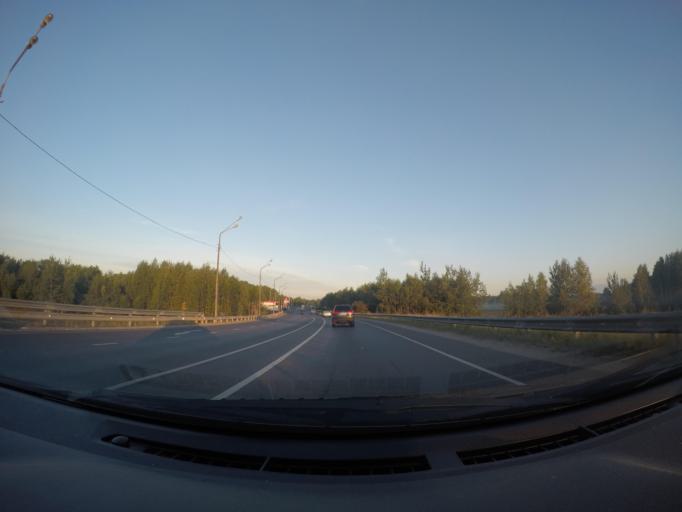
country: RU
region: Moskovskaya
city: Kratovo
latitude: 55.6400
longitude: 38.1785
